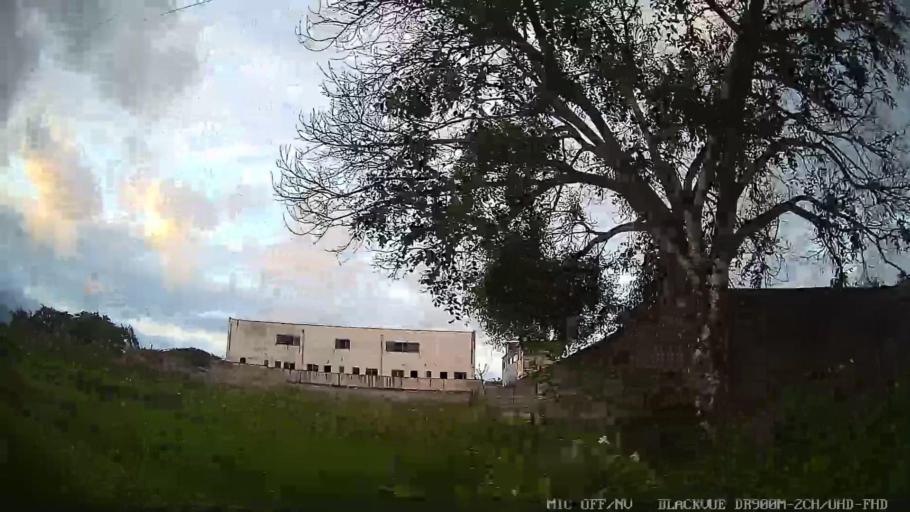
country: BR
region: Sao Paulo
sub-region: Itanhaem
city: Itanhaem
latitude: -24.1877
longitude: -46.8363
